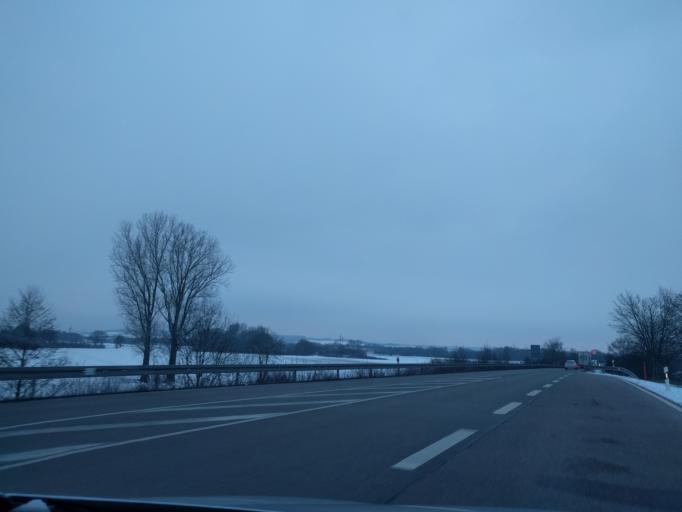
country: DE
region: Bavaria
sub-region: Swabia
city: Donauwoerth
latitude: 48.6991
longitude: 10.7920
